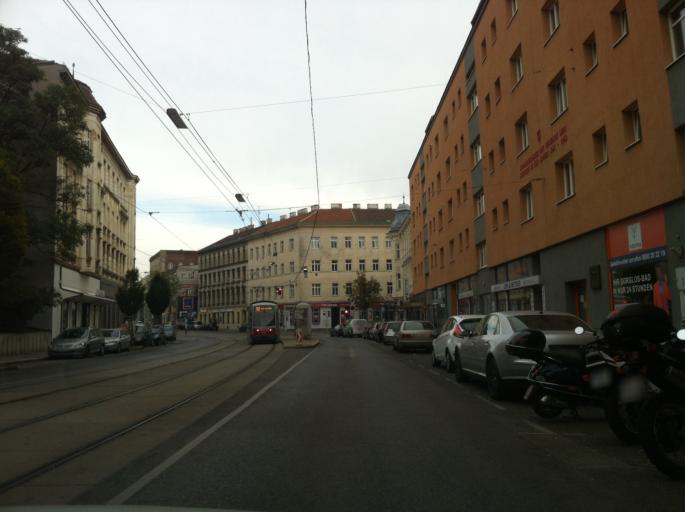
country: AT
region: Lower Austria
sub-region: Politischer Bezirk Modling
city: Perchtoldsdorf
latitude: 48.1945
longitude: 16.2834
